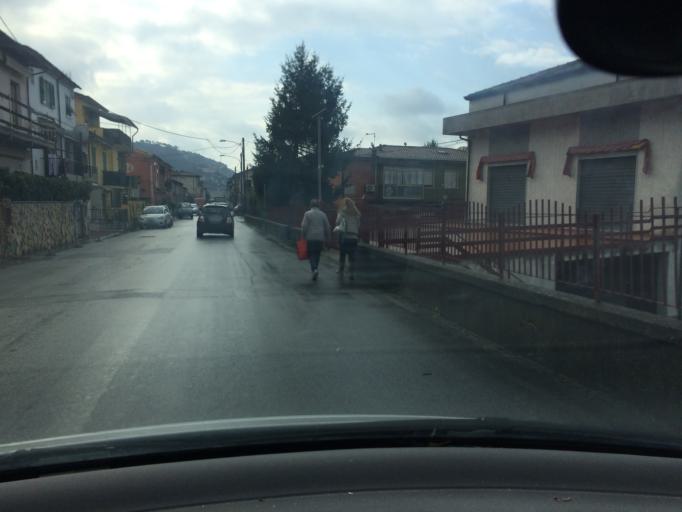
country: IT
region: Tuscany
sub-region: Provincia di Massa-Carrara
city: Massa
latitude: 44.0460
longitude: 10.1338
